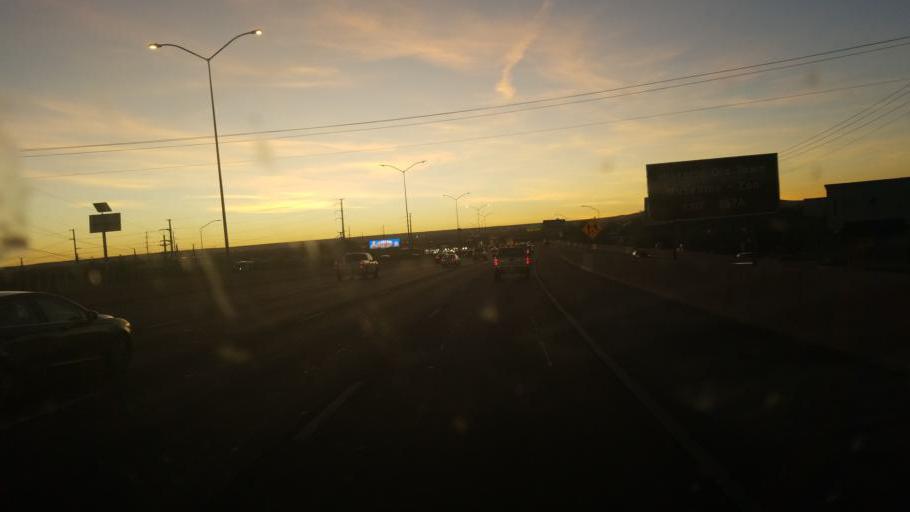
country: US
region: New Mexico
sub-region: Bernalillo County
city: Albuquerque
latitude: 35.1064
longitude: -106.6596
